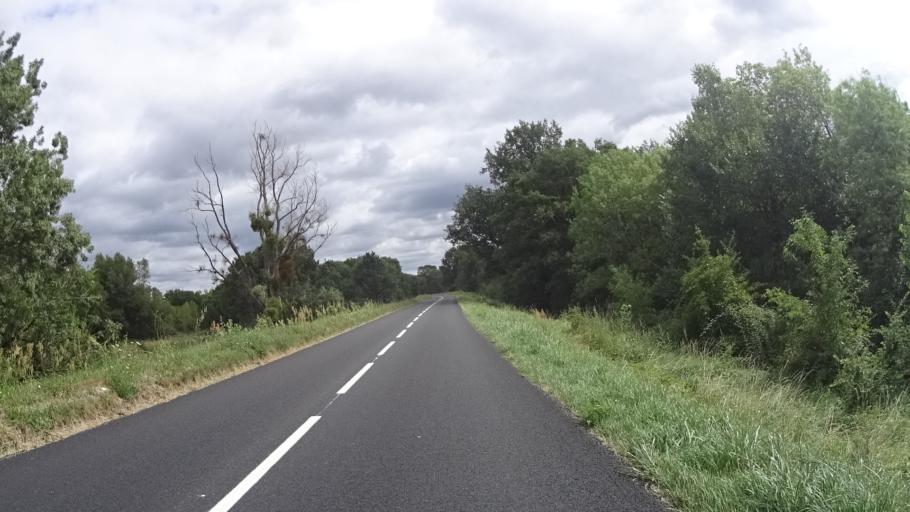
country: FR
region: Centre
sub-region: Departement d'Indre-et-Loire
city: Cheille
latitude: 47.2888
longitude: 0.3421
